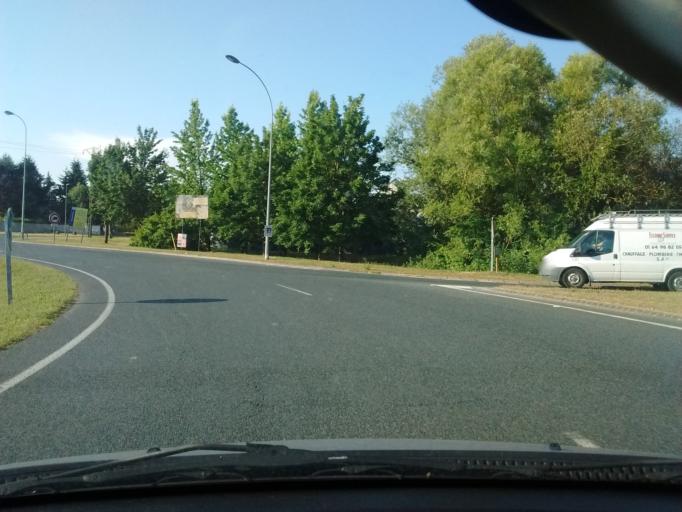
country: FR
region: Ile-de-France
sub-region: Departement de l'Essonne
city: Milly-la-Foret
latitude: 48.4117
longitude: 2.4655
